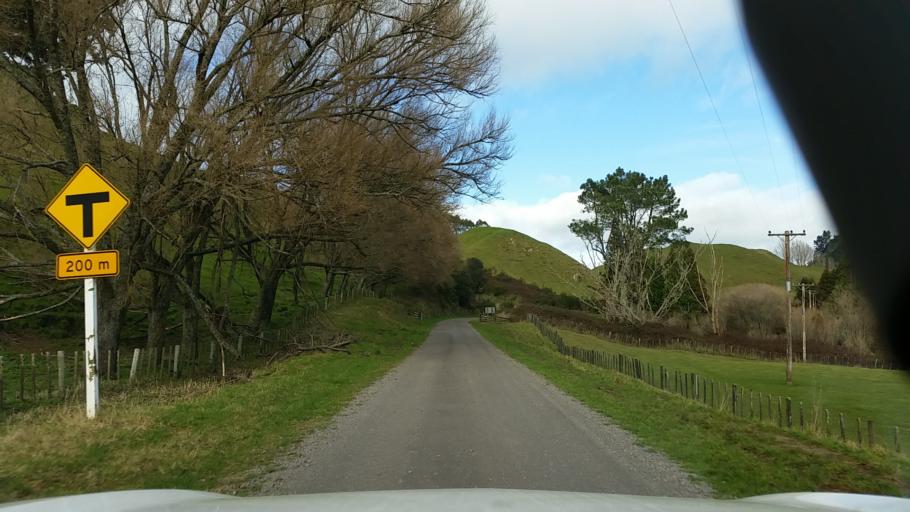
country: NZ
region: Waikato
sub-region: Taupo District
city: Taupo
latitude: -38.4633
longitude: 176.2416
